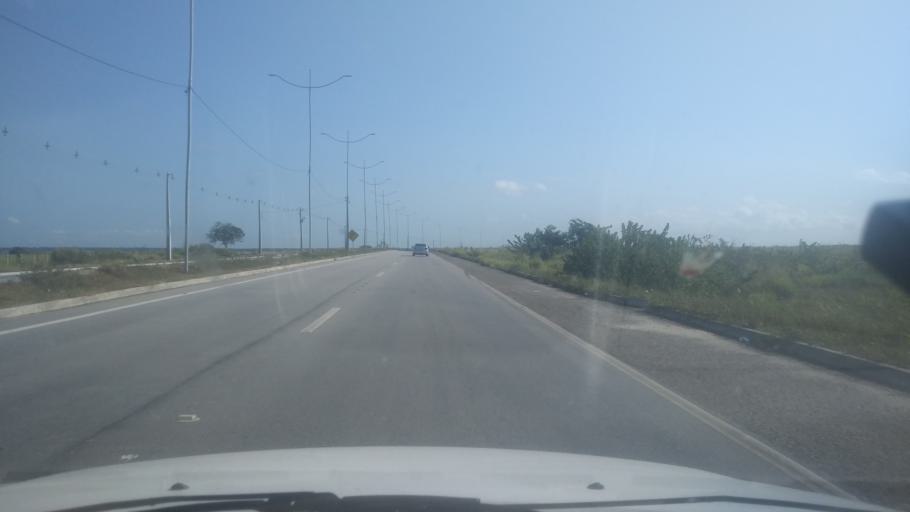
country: BR
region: Rio Grande do Norte
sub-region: Macaiba
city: Macaiba
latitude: -5.8283
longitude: -35.3700
